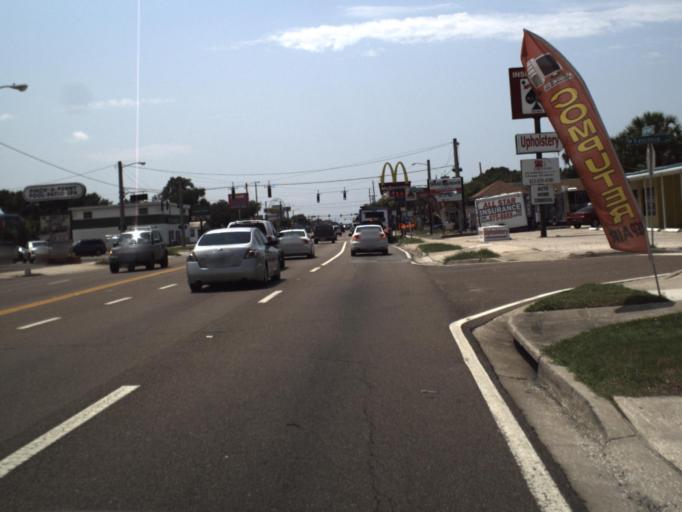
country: US
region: Florida
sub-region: Hillsborough County
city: Tampa
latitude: 27.9126
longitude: -82.5061
